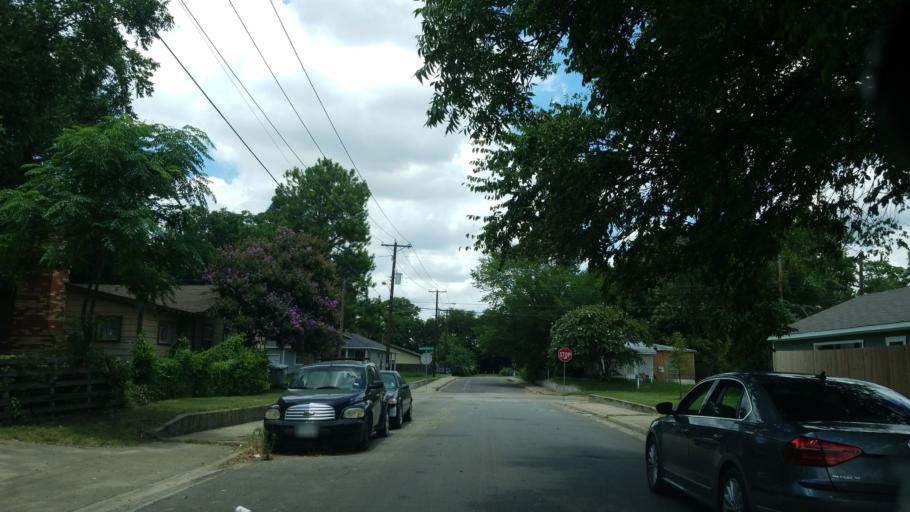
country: US
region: Texas
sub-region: Dallas County
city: Dallas
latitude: 32.7414
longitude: -96.7508
